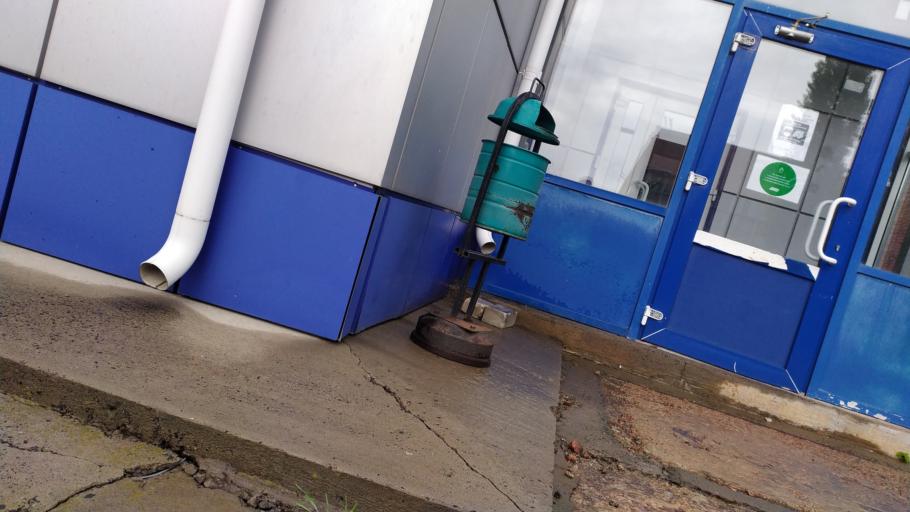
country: RU
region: Kursk
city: Kursk
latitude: 51.7617
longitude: 36.1268
